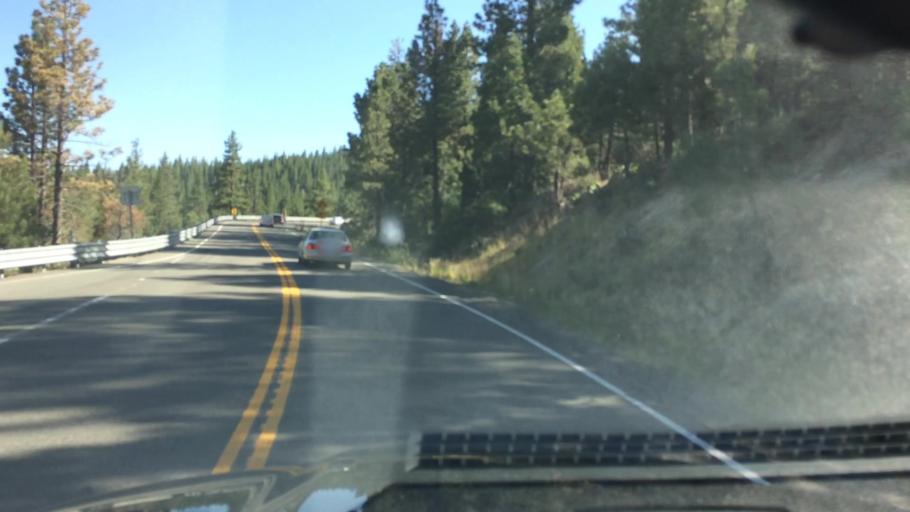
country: US
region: Nevada
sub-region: Washoe County
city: Incline Village
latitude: 39.3390
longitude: -119.8609
